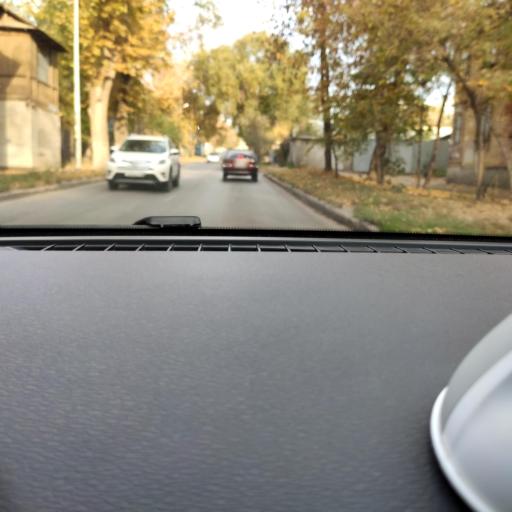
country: RU
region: Samara
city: Samara
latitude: 53.2396
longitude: 50.2589
